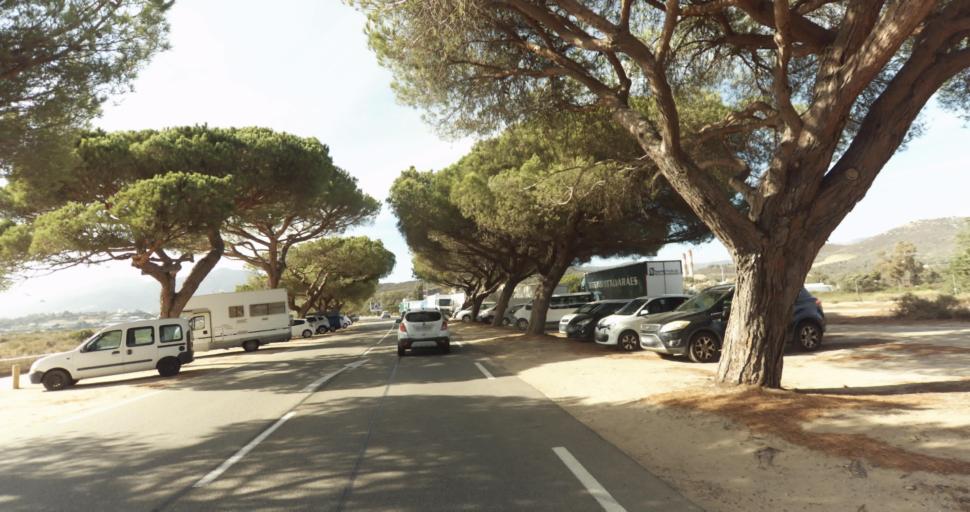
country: FR
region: Corsica
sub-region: Departement de la Corse-du-Sud
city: Ajaccio
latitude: 41.9236
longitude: 8.7843
